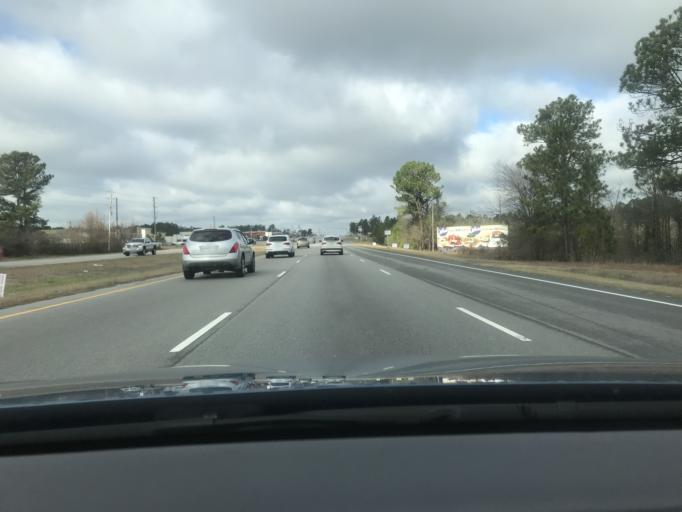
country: US
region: North Carolina
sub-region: Cumberland County
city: Spring Lake
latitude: 35.2555
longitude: -79.0346
